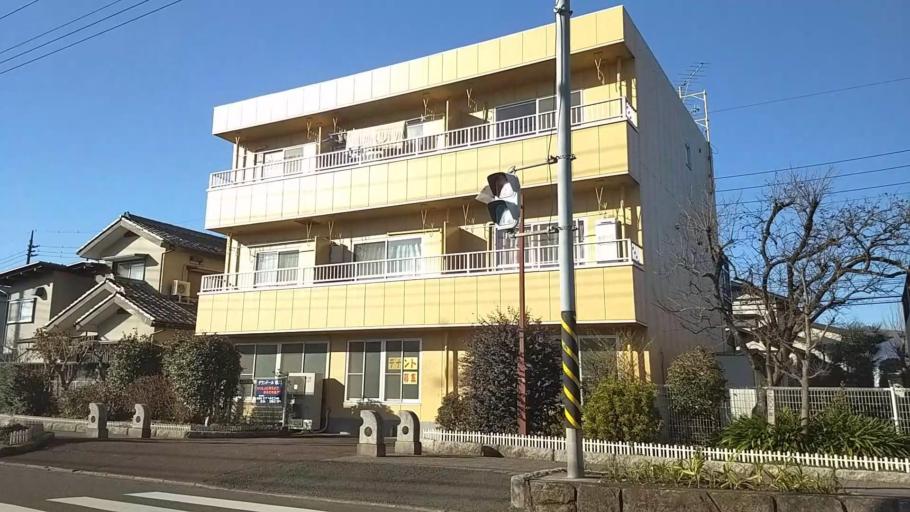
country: JP
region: Kanagawa
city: Atsugi
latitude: 35.4323
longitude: 139.3598
